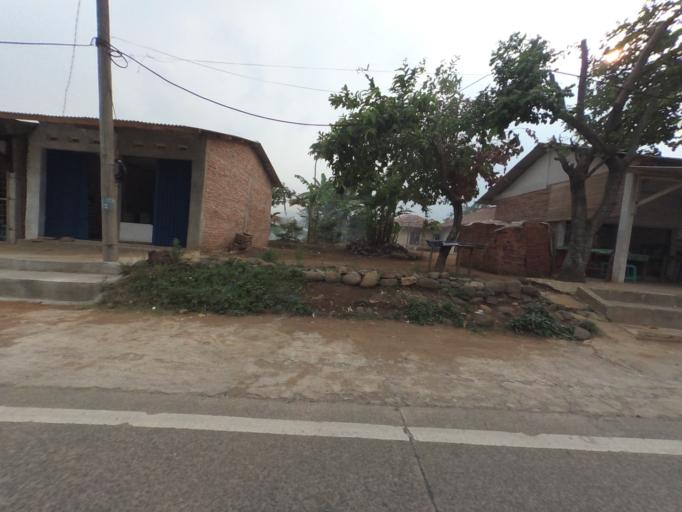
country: ID
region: West Java
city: Sidoger Lebak
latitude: -6.5613
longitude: 106.5777
